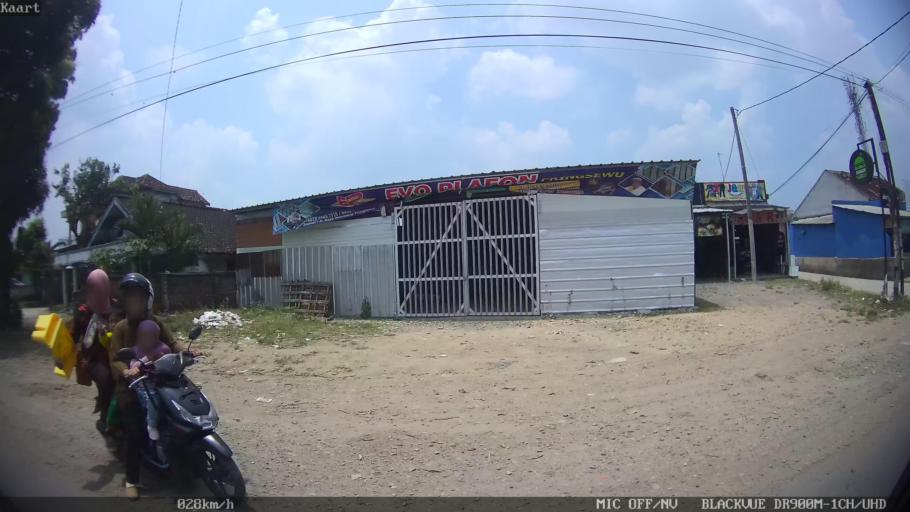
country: ID
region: Lampung
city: Pringsewu
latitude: -5.3620
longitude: 104.9982
